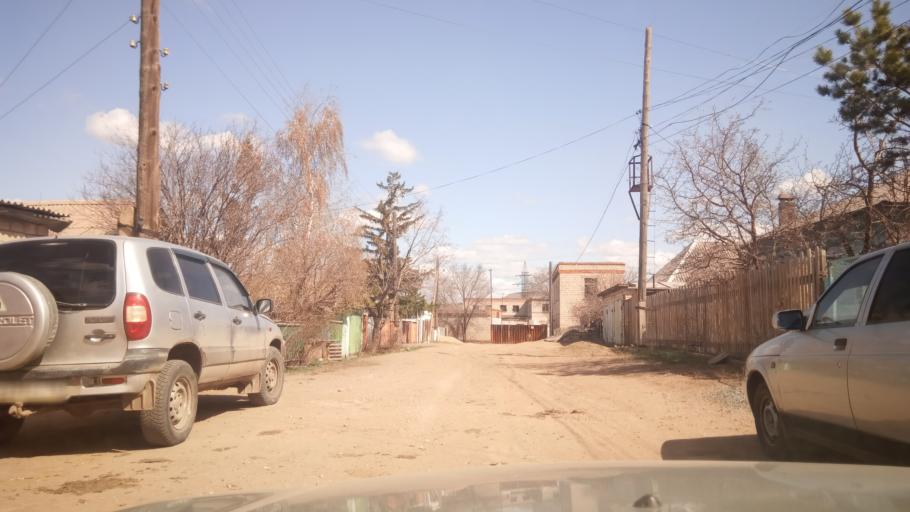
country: RU
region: Orenburg
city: Novotroitsk
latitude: 51.2093
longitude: 58.3170
